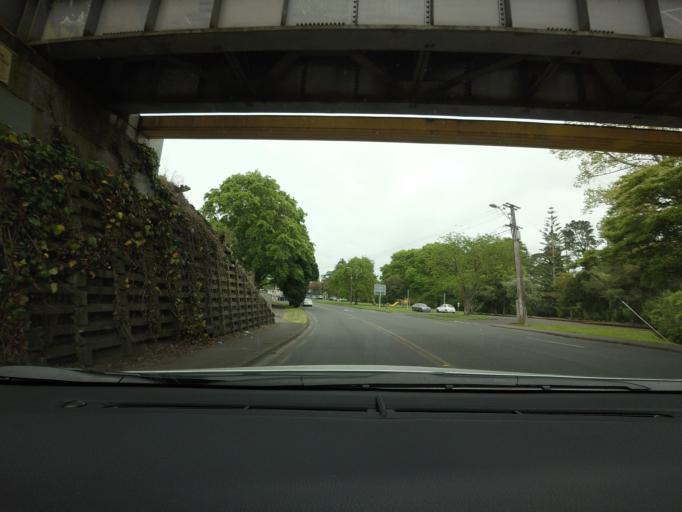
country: NZ
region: Auckland
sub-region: Auckland
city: Rosebank
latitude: -36.8787
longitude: 174.6302
